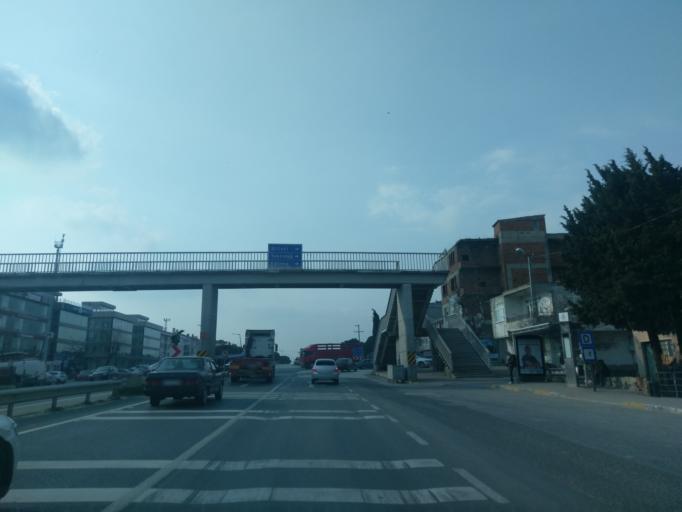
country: TR
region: Istanbul
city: Selimpasa
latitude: 41.0565
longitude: 28.3687
